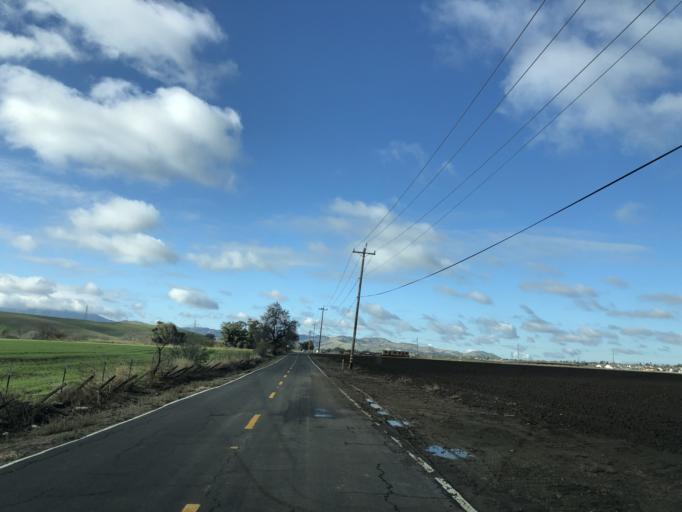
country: US
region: California
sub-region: Contra Costa County
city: Brentwood
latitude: 37.9471
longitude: -121.7466
